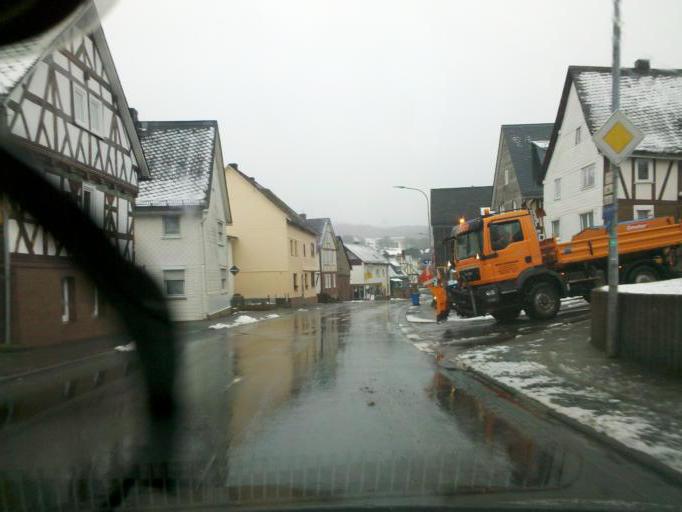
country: DE
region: Hesse
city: Dillenburg
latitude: 50.8127
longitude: 8.2726
